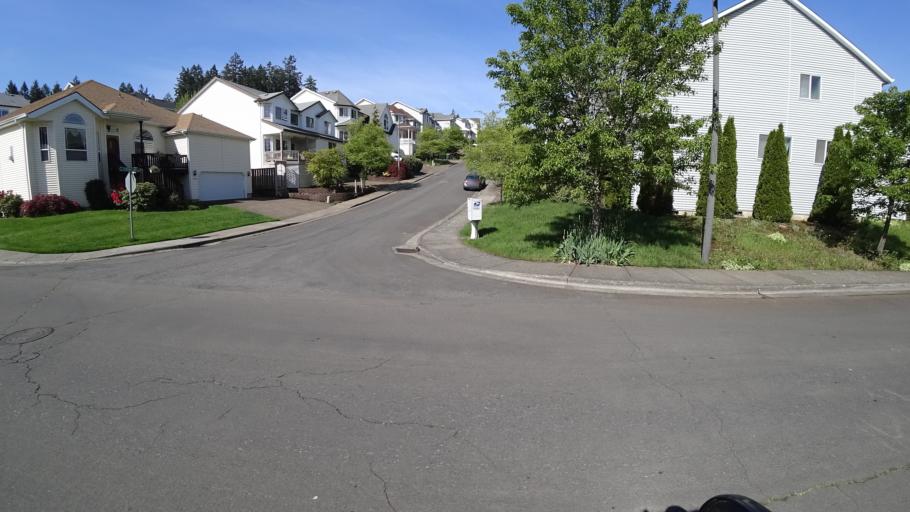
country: US
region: Oregon
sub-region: Washington County
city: Aloha
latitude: 45.4542
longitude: -122.8439
